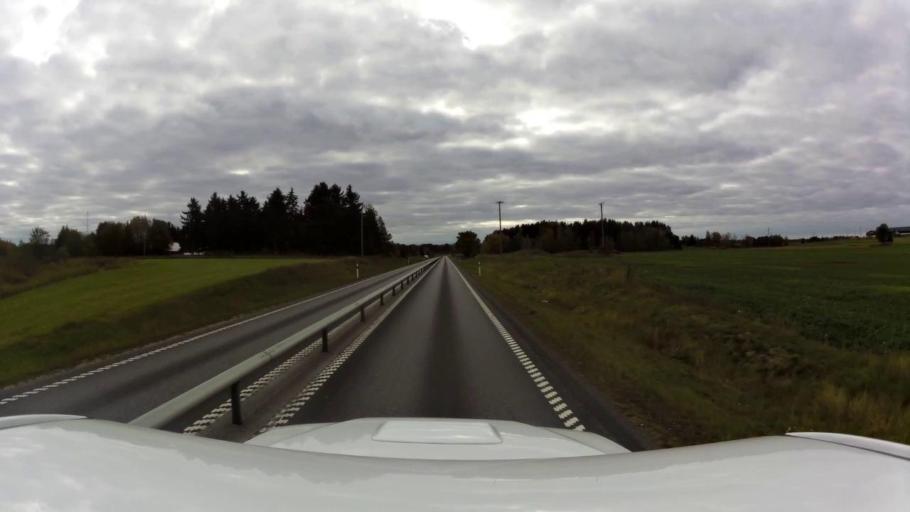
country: SE
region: OEstergoetland
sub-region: Linkopings Kommun
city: Malmslatt
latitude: 58.3280
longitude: 15.5638
